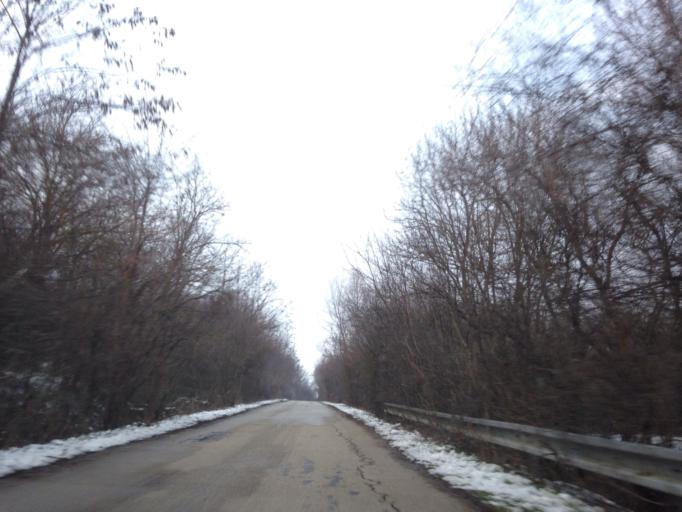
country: SK
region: Nitriansky
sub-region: Okres Nitra
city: Vrable
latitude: 48.0768
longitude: 18.3715
